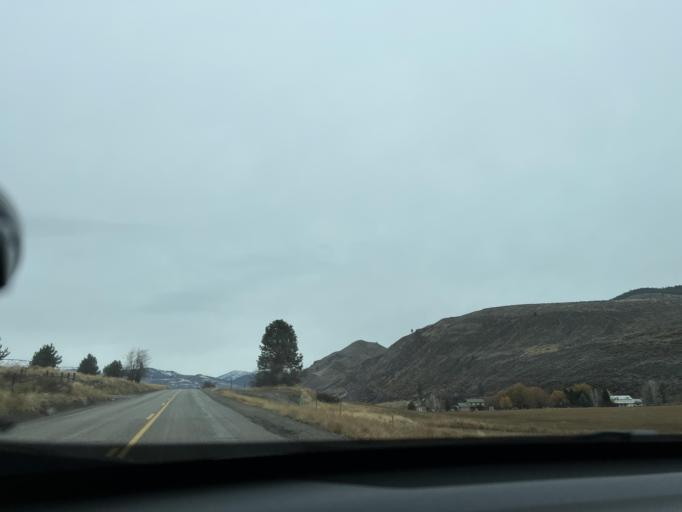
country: US
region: Washington
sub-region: Okanogan County
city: Brewster
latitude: 48.5116
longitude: -120.1740
